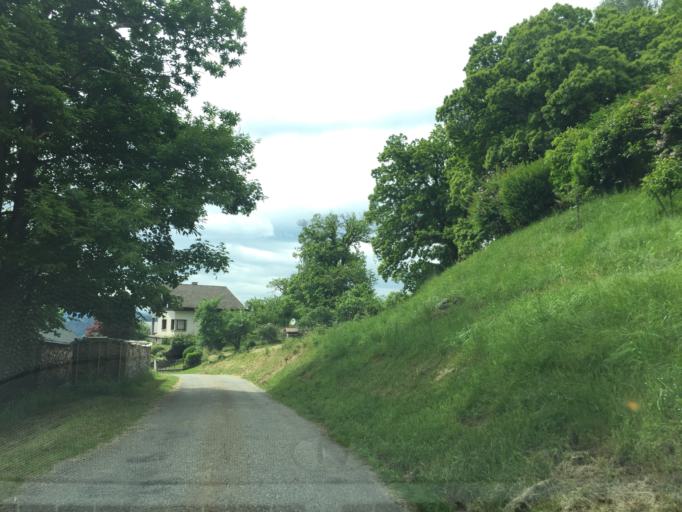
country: FR
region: Rhone-Alpes
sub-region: Departement de la Savoie
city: La Rochette
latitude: 45.4472
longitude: 6.1480
